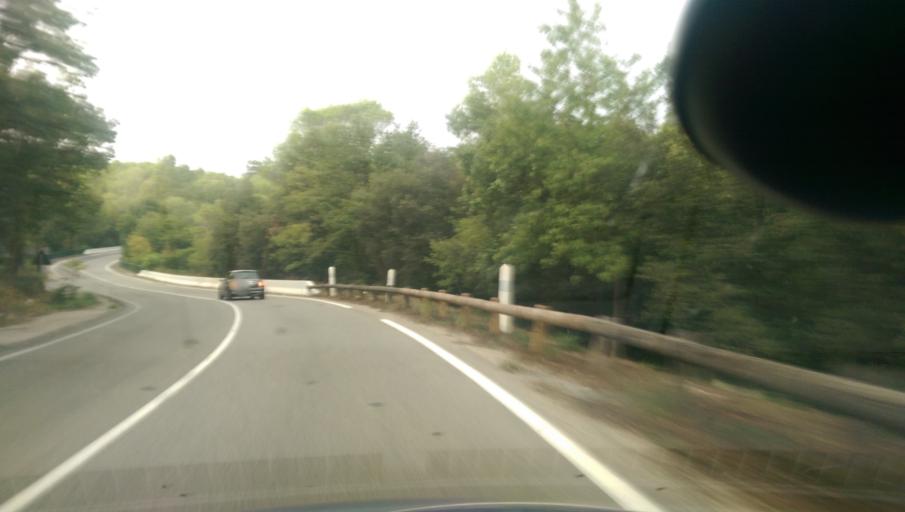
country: FR
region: Provence-Alpes-Cote d'Azur
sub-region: Departement des Alpes-Maritimes
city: Biot
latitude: 43.6342
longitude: 7.0510
